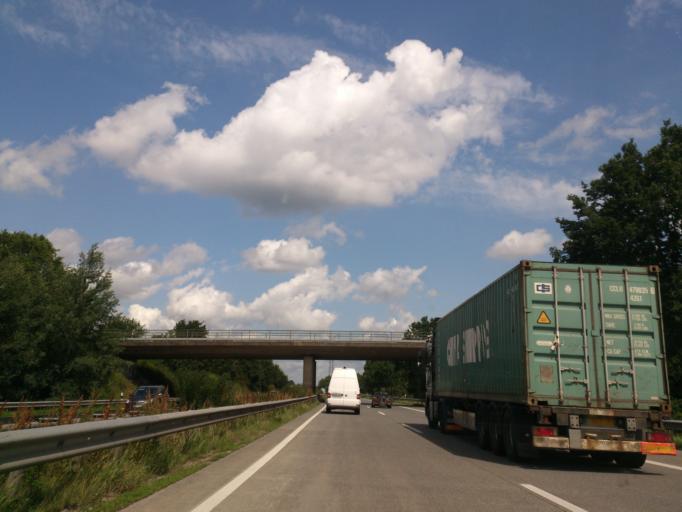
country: DE
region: Schleswig-Holstein
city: Kolln-Reisiek
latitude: 53.7769
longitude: 9.7062
